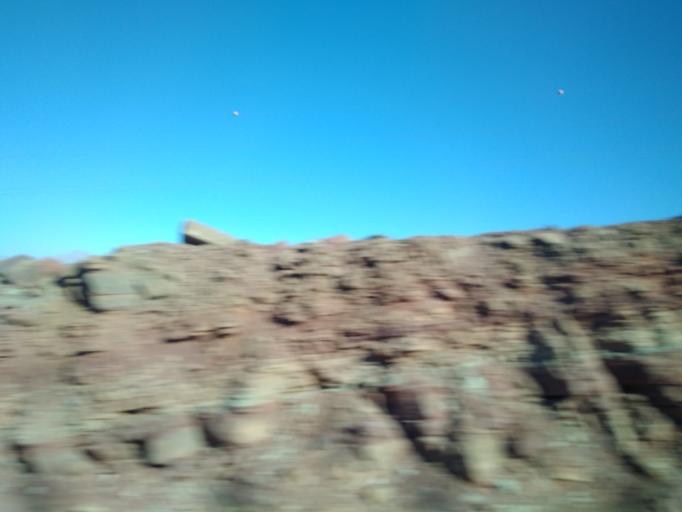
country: IL
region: Southern District
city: Eilat
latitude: 29.6016
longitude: 34.8702
